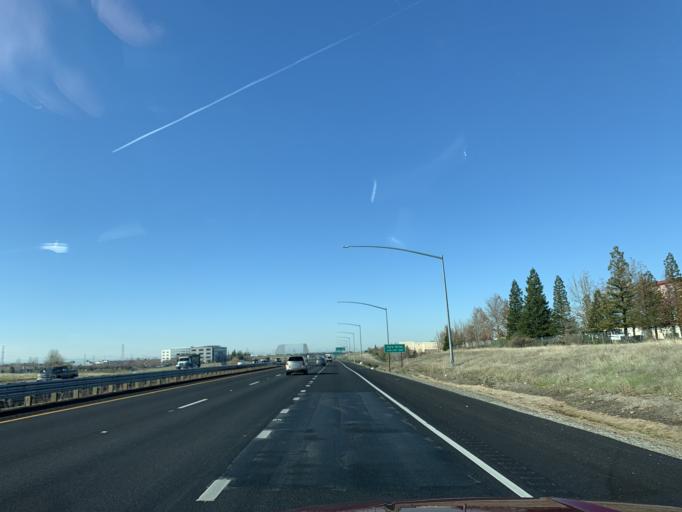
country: US
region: California
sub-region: Placer County
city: Roseville
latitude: 38.7819
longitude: -121.2744
